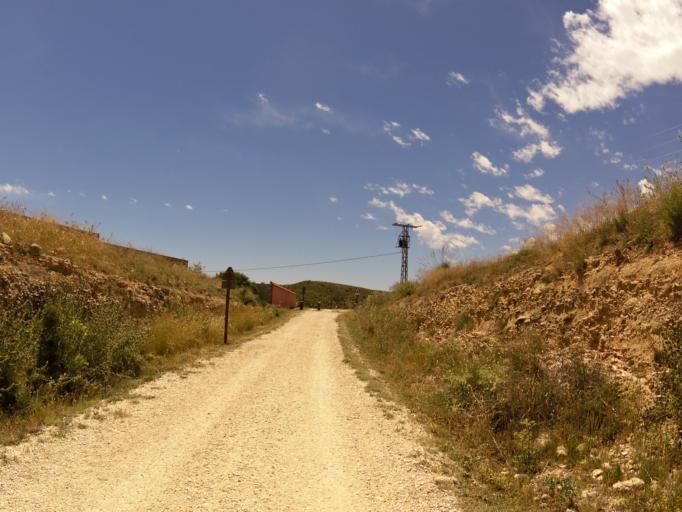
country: ES
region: Valencia
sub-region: Provincia de Alicante
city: Agost
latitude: 38.4483
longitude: -0.6746
